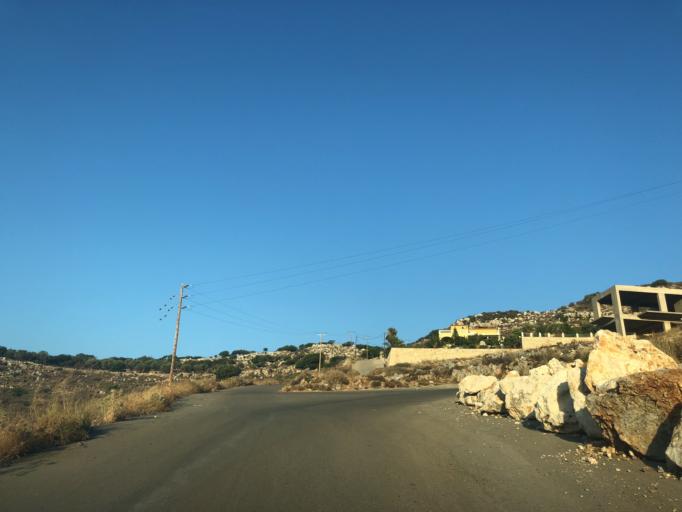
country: GR
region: Crete
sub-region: Nomos Rethymnis
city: Atsipopoulon
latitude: 35.3592
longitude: 24.3929
